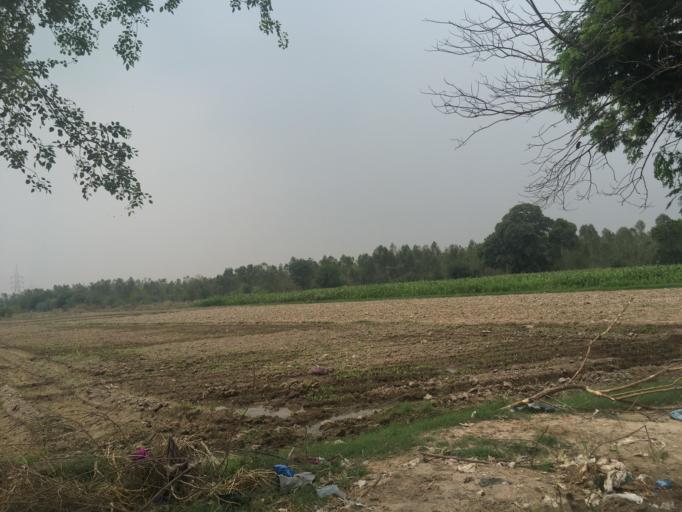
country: PK
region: Punjab
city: Lahore
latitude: 31.6258
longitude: 74.3479
